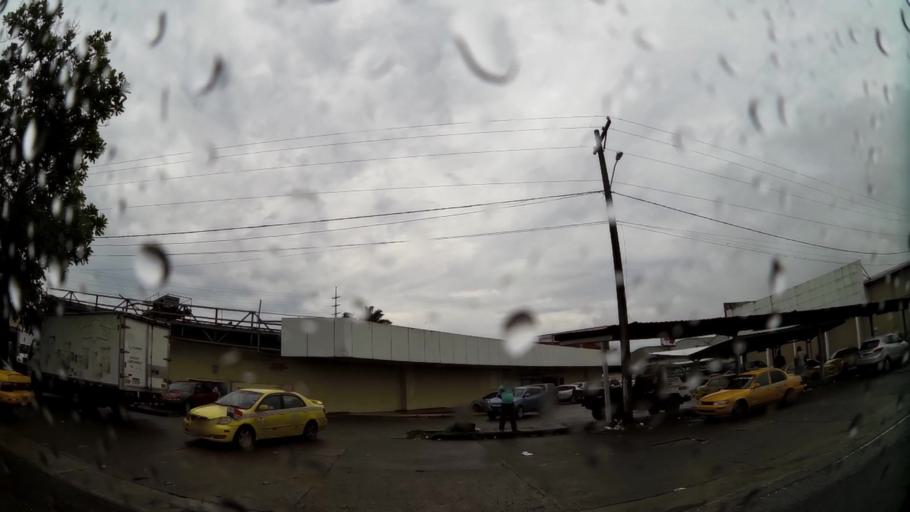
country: PA
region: Colon
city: Arco Iris
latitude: 9.3402
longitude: -79.8709
